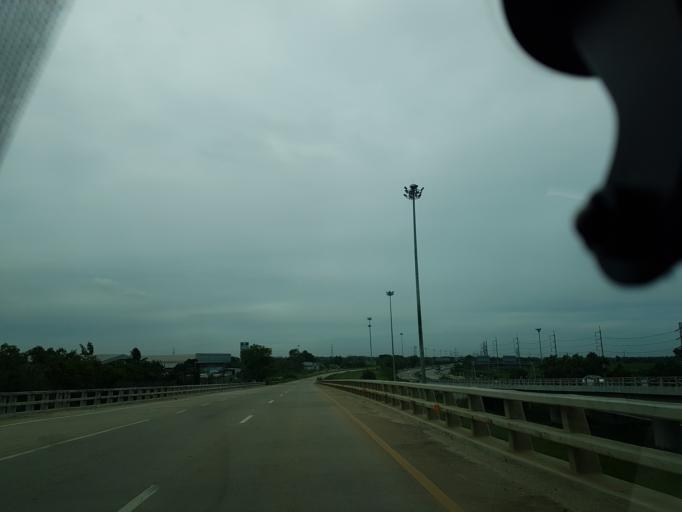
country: TH
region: Phra Nakhon Si Ayutthaya
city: Bang Pa-in
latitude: 14.1561
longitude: 100.5682
